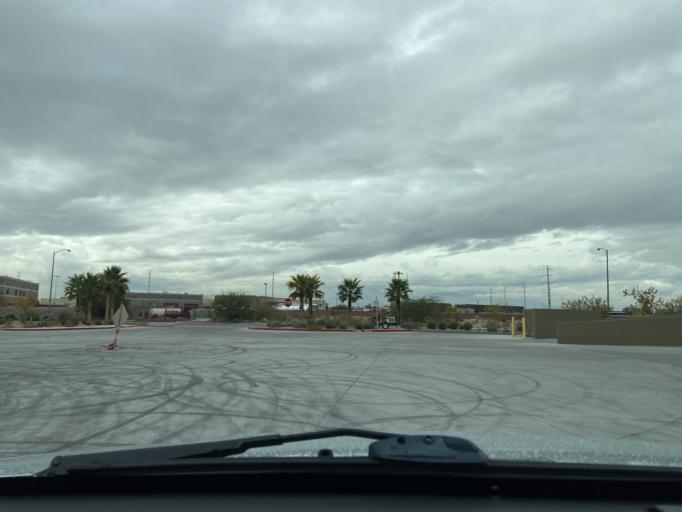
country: US
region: Nevada
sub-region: Clark County
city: North Las Vegas
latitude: 36.2458
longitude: -115.1116
